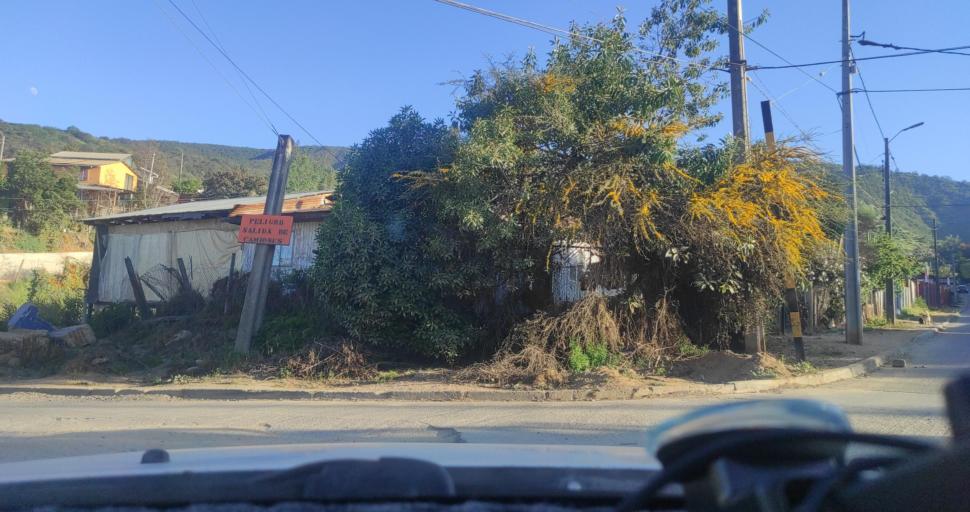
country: CL
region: Valparaiso
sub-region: Provincia de Marga Marga
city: Limache
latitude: -32.9882
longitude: -71.2358
